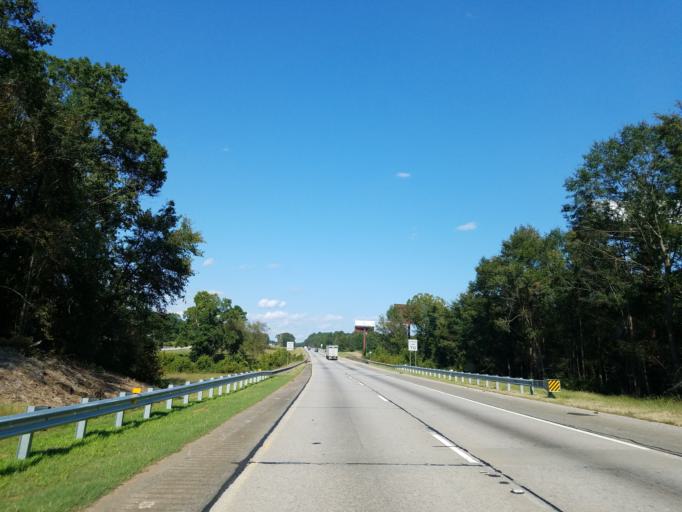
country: US
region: Georgia
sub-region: Jackson County
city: Commerce
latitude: 34.2611
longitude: -83.4519
